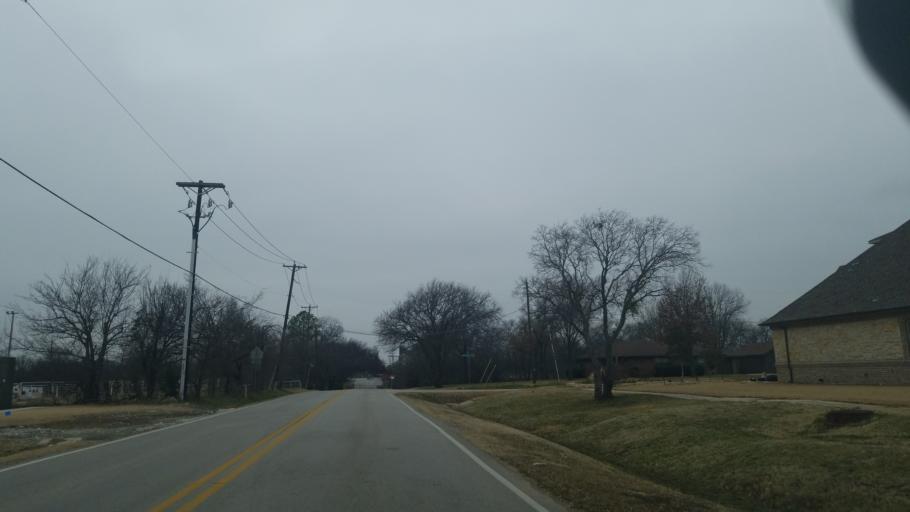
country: US
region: Texas
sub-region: Denton County
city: Denton
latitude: 33.1616
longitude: -97.1384
